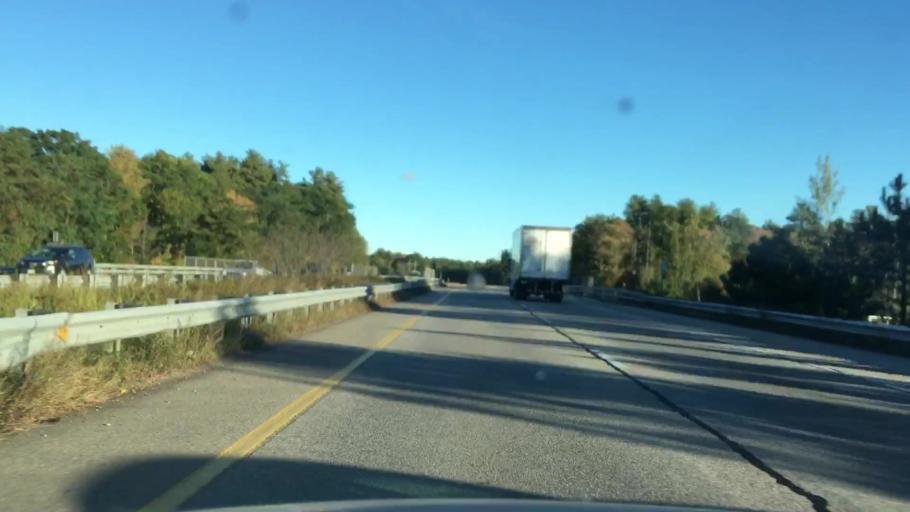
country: US
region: New Hampshire
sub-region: Rockingham County
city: Epping
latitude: 43.0113
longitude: -71.0104
